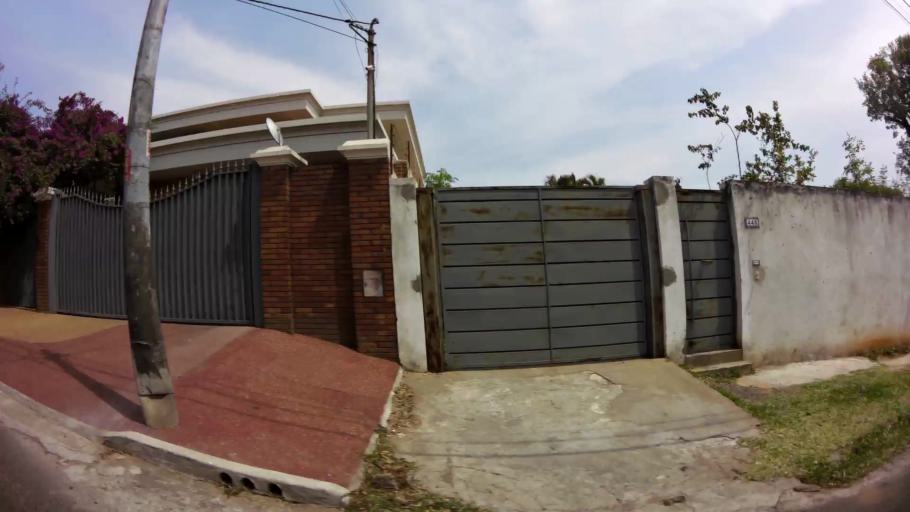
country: PY
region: Asuncion
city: Asuncion
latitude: -25.2784
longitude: -57.5972
